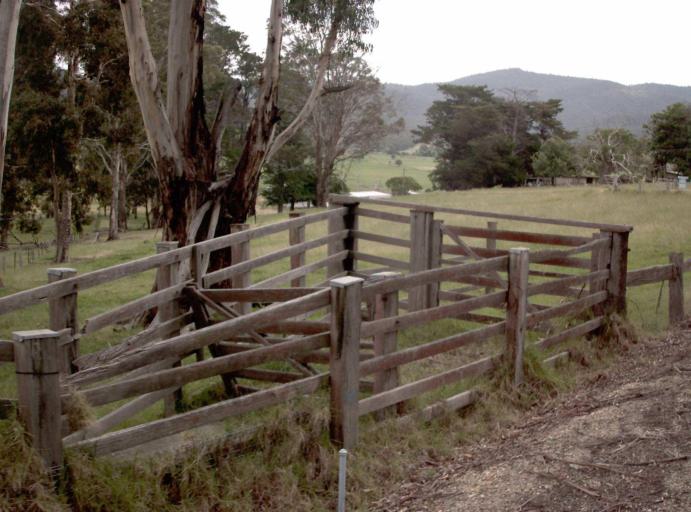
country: AU
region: New South Wales
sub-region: Bombala
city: Bombala
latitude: -37.4862
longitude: 149.1813
